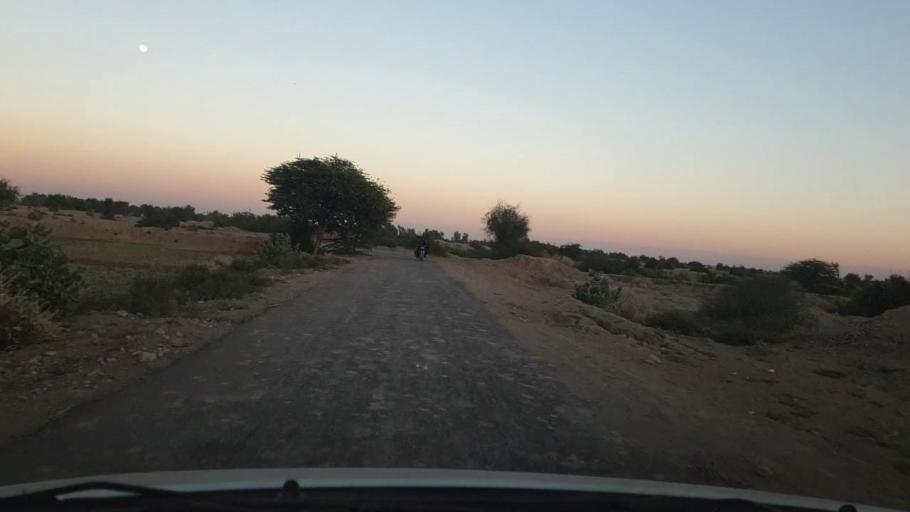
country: PK
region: Sindh
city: Johi
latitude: 26.8291
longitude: 67.4586
